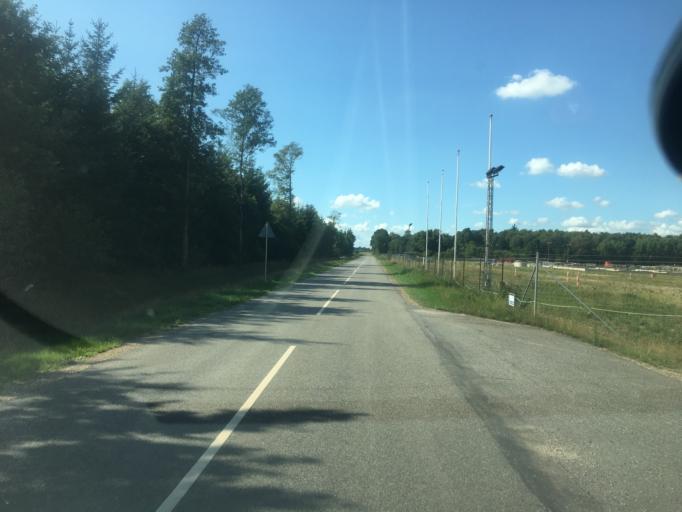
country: DE
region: Schleswig-Holstein
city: Ellhoft
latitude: 54.9650
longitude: 8.9774
